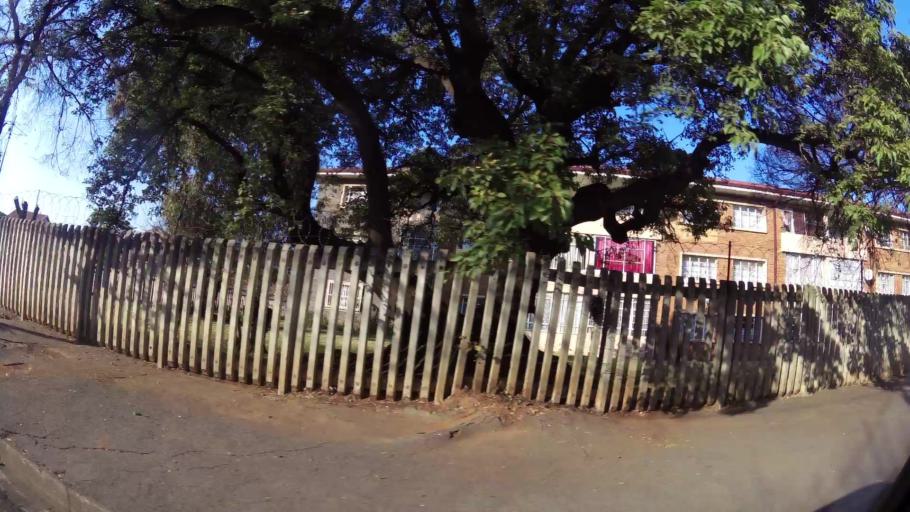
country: ZA
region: Gauteng
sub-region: Ekurhuleni Metropolitan Municipality
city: Germiston
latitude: -26.2030
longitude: 28.1320
